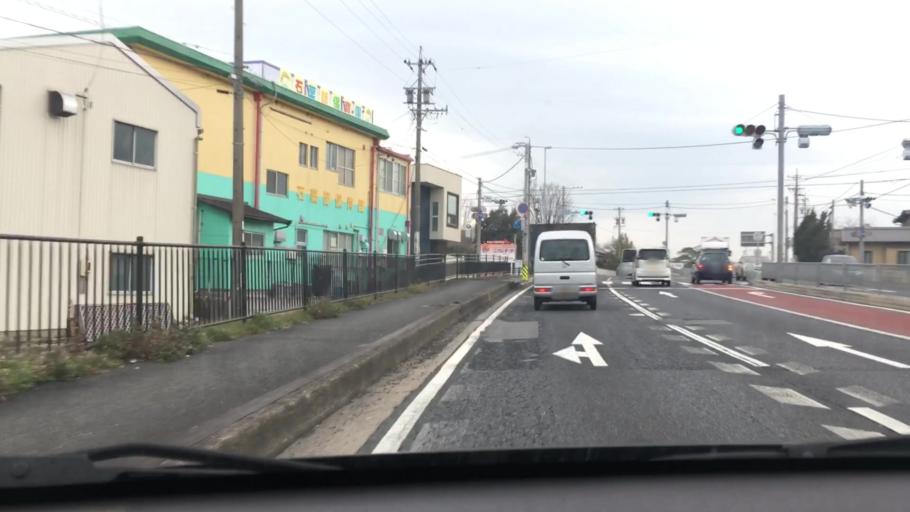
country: JP
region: Mie
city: Suzuka
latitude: 34.9020
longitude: 136.5485
